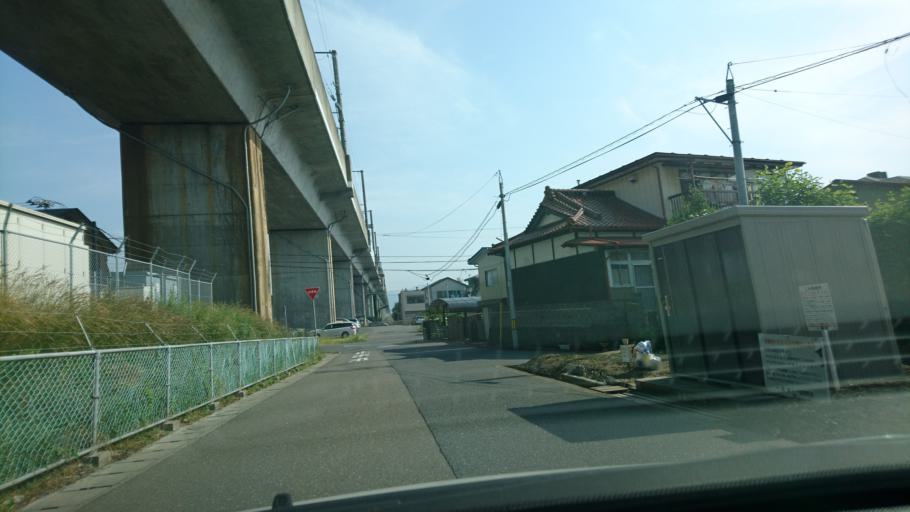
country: JP
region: Iwate
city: Ichinoseki
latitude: 38.9296
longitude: 141.1406
